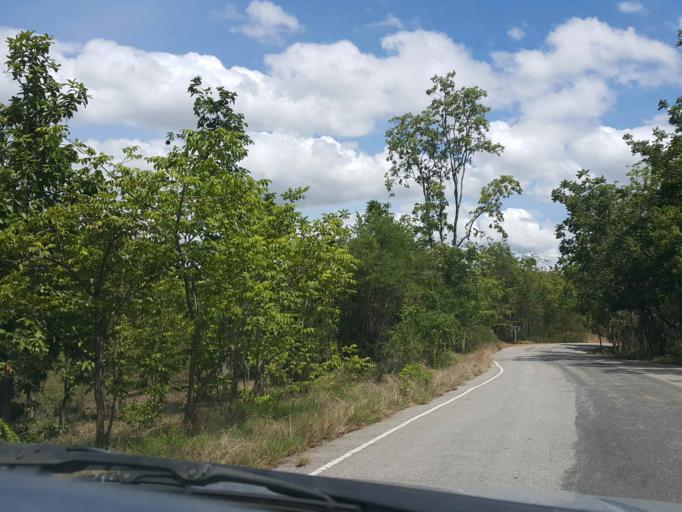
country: TH
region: Chiang Mai
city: Doi Lo
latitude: 18.4948
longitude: 98.7565
